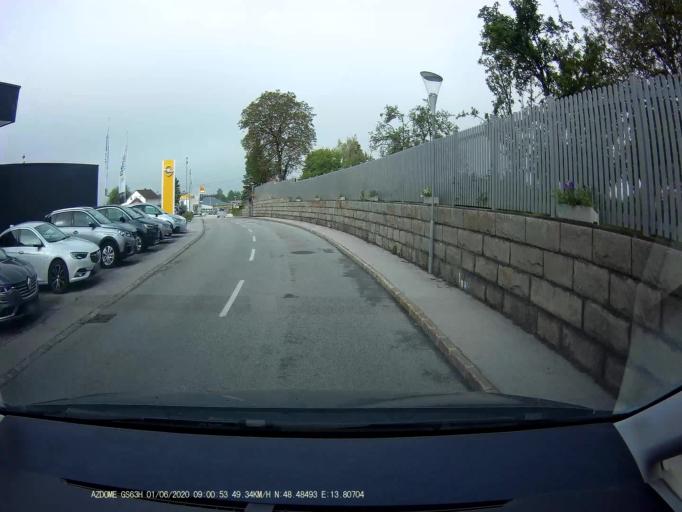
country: AT
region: Upper Austria
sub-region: Politischer Bezirk Rohrbach
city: Pfarrkirchen im Muehlkreis
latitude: 48.4849
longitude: 13.8066
